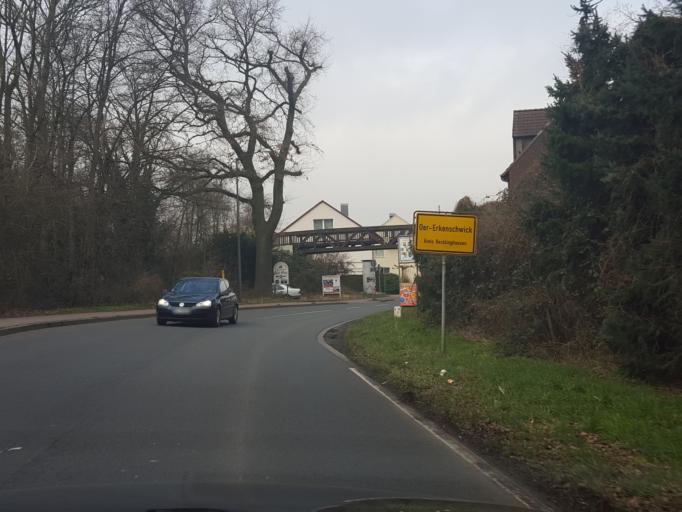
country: DE
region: North Rhine-Westphalia
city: Oer-Erkenschwick
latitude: 51.6448
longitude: 7.2327
